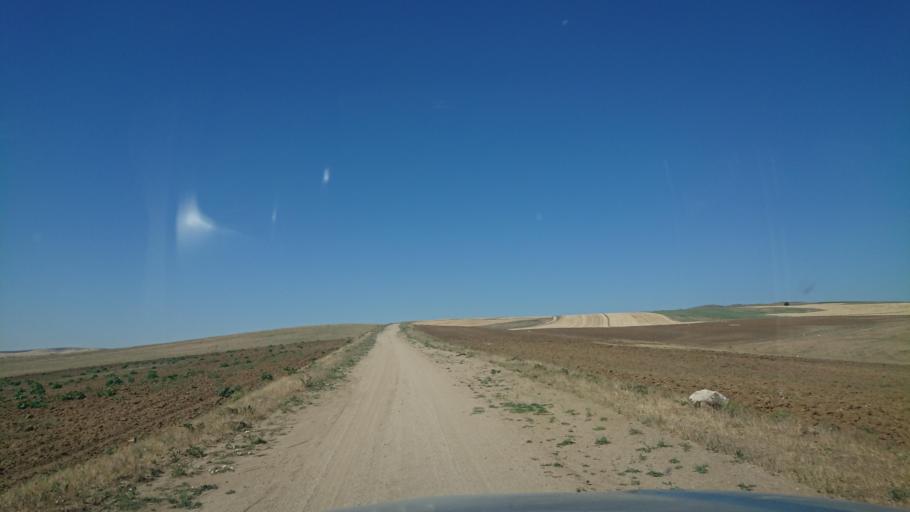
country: TR
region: Aksaray
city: Sariyahsi
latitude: 38.9293
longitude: 33.8558
